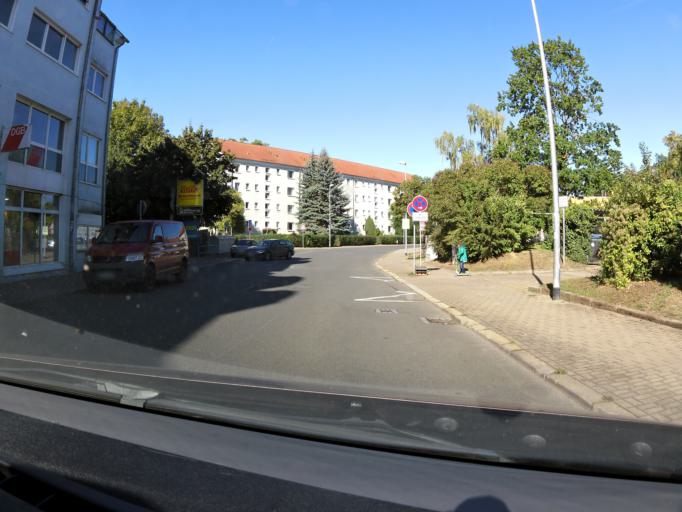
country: DE
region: Thuringia
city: Nordhausen
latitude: 51.4989
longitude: 10.7918
